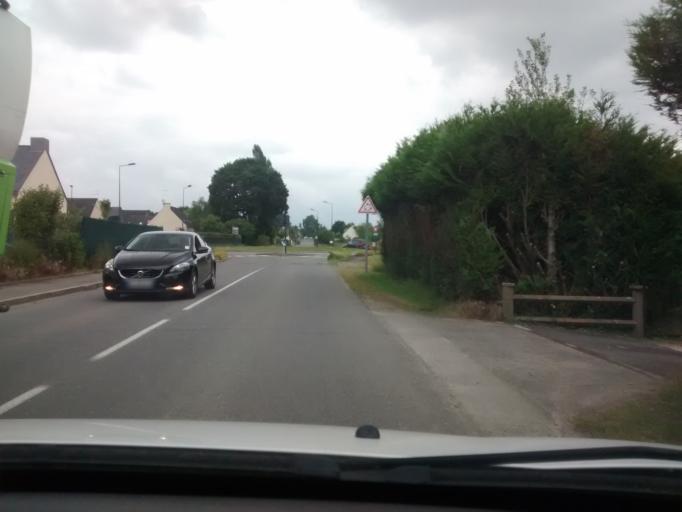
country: FR
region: Brittany
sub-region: Departement d'Ille-et-Vilaine
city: Liffre
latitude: 48.2050
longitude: -1.5098
